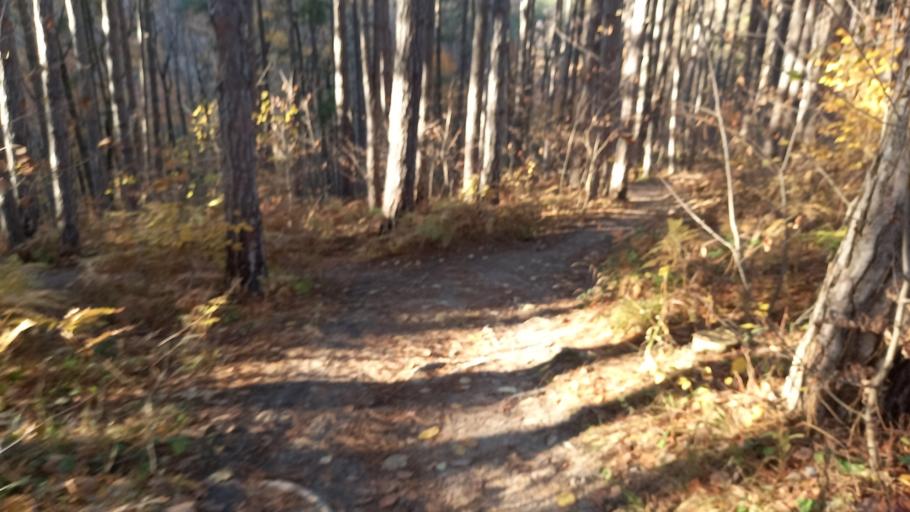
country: RU
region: Krasnodarskiy
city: Goryachiy Klyuch
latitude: 44.6122
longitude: 39.1036
